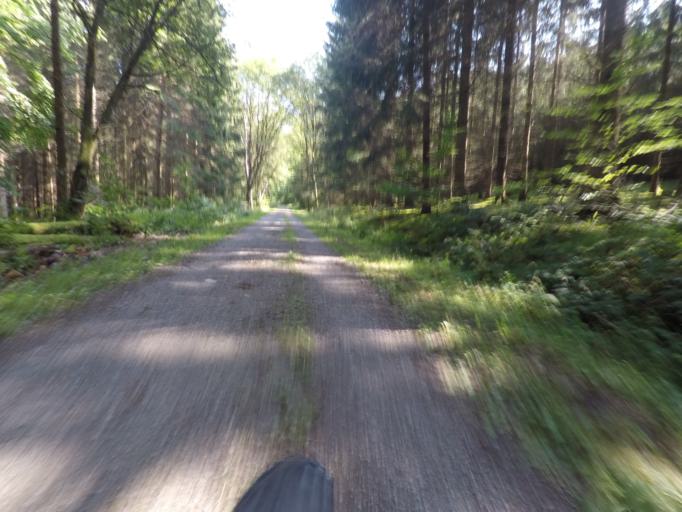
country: DE
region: Baden-Wuerttemberg
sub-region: Regierungsbezirk Stuttgart
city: Steinenbronn
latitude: 48.6804
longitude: 9.1017
